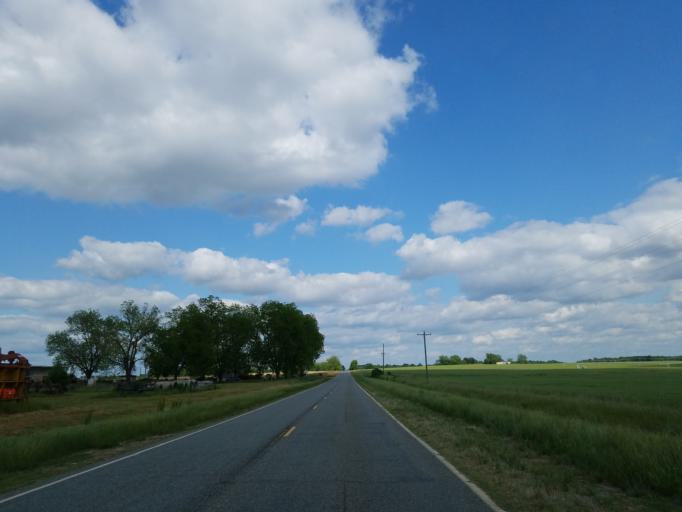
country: US
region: Georgia
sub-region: Dooly County
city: Unadilla
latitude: 32.2589
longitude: -83.7898
